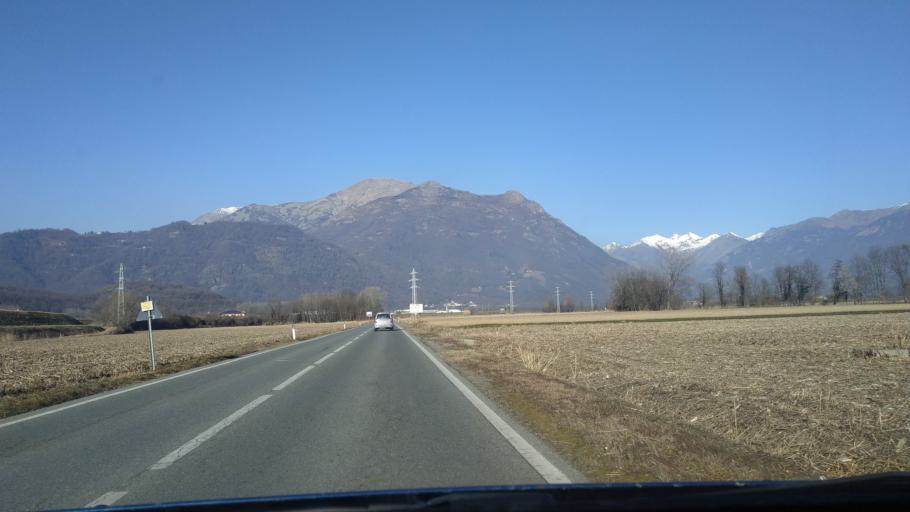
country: IT
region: Piedmont
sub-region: Provincia di Torino
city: Fiorano Canavese
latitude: 45.4681
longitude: 7.8417
